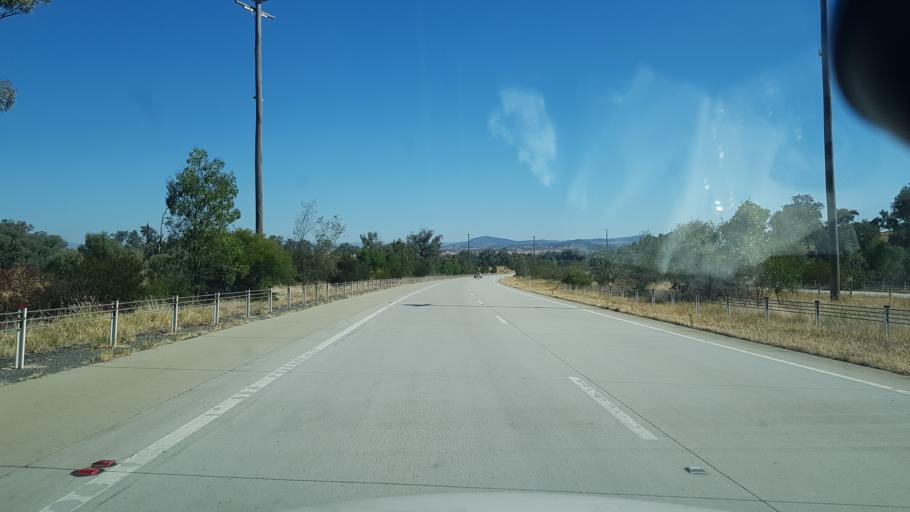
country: AU
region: New South Wales
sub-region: Albury Municipality
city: Lavington
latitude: -35.9230
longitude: 147.0927
